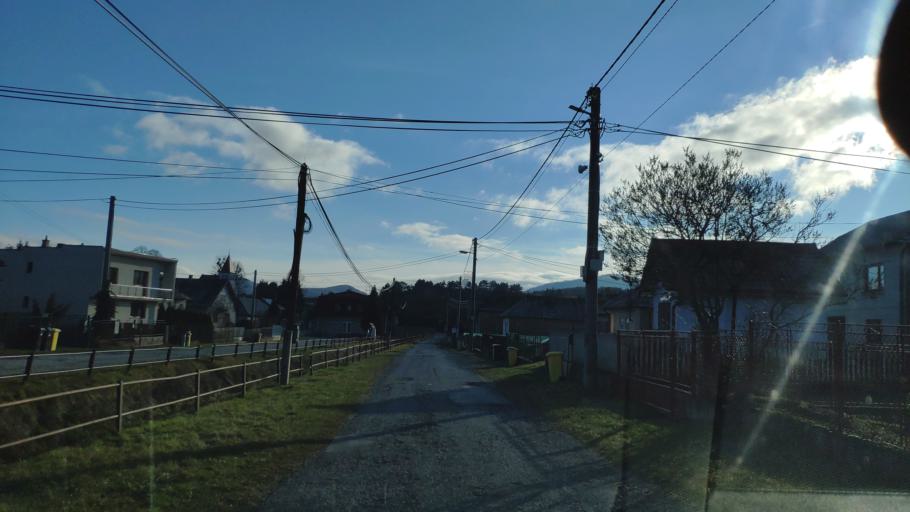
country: SK
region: Presovsky
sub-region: Okres Presov
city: Presov
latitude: 48.9164
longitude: 21.1430
